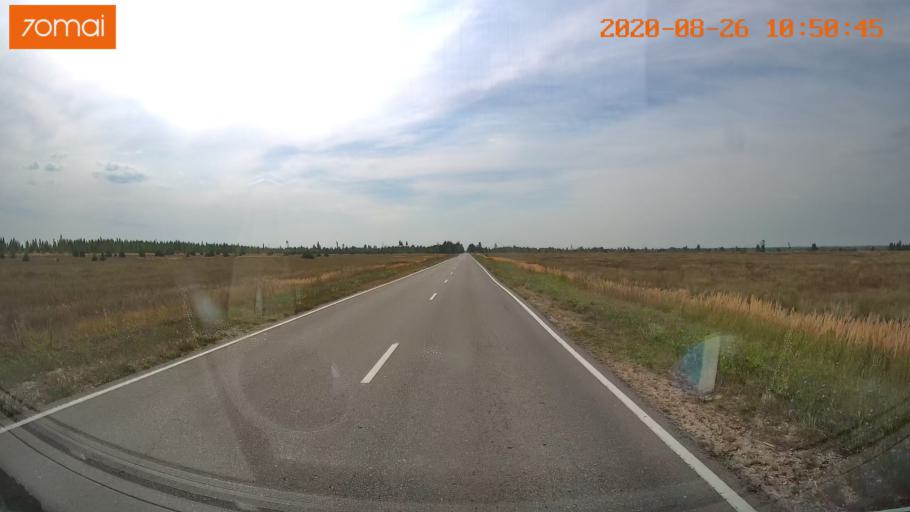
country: RU
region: Rjazan
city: Lashma
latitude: 54.6830
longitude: 41.1561
